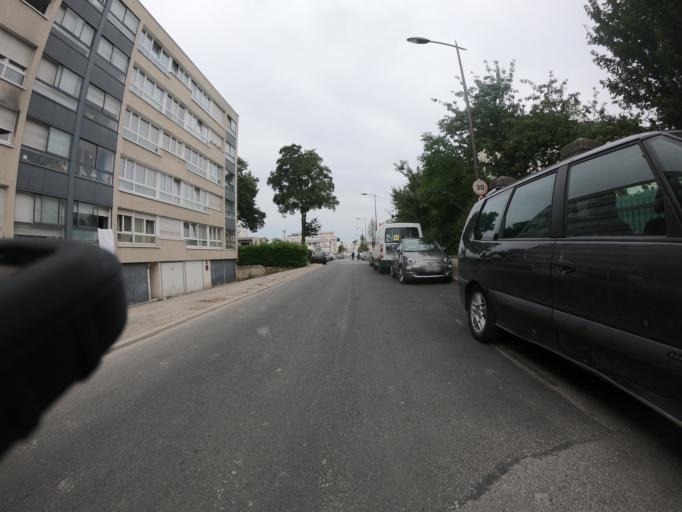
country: FR
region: Ile-de-France
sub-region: Departement du Val-de-Marne
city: Thiais
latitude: 48.7638
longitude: 2.3843
